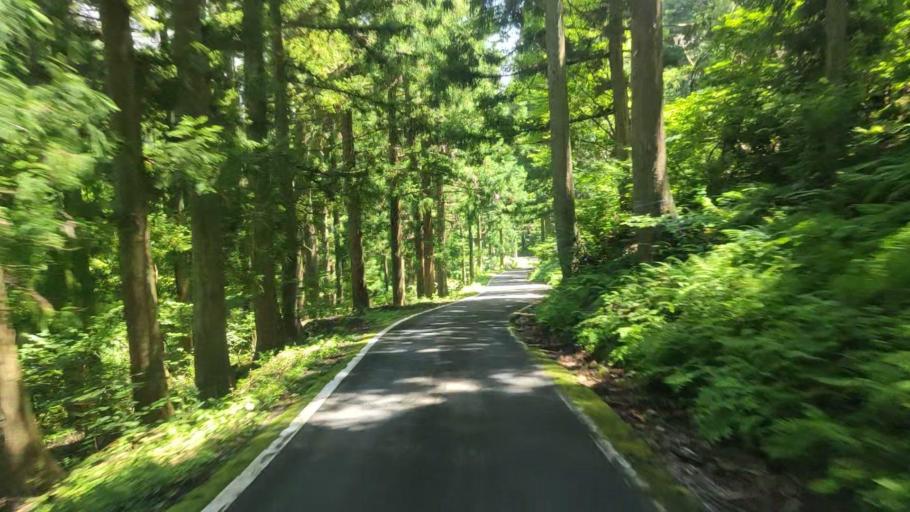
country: JP
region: Fukui
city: Ono
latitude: 35.7633
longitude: 136.5541
